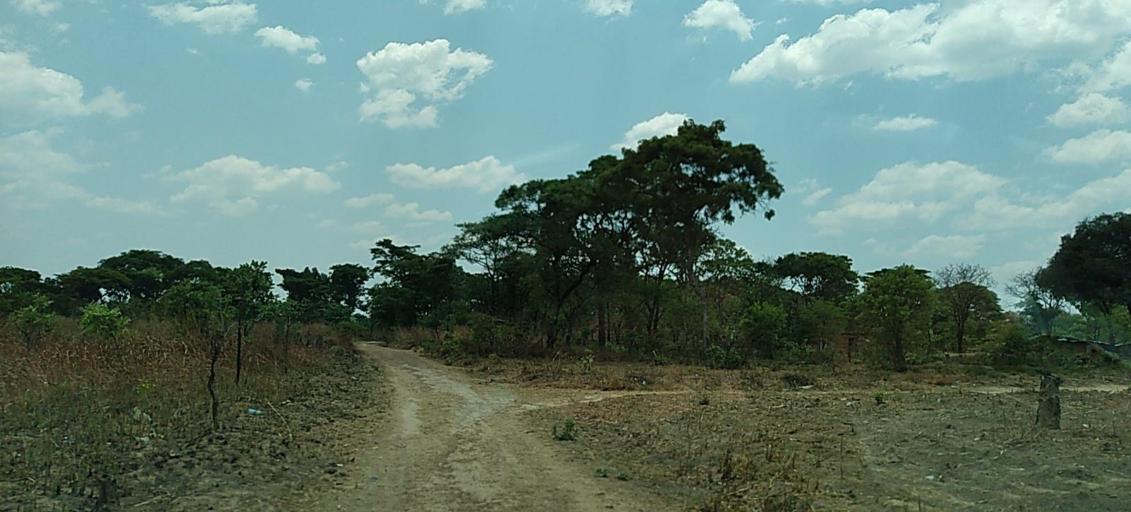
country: ZM
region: Copperbelt
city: Chililabombwe
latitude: -12.4549
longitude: 27.6728
